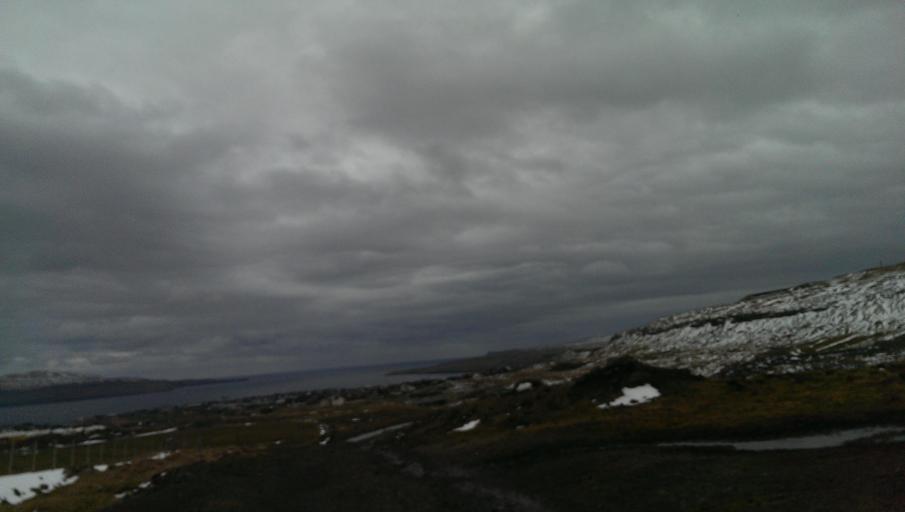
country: FO
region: Streymoy
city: Hoyvik
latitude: 62.0369
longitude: -6.8034
